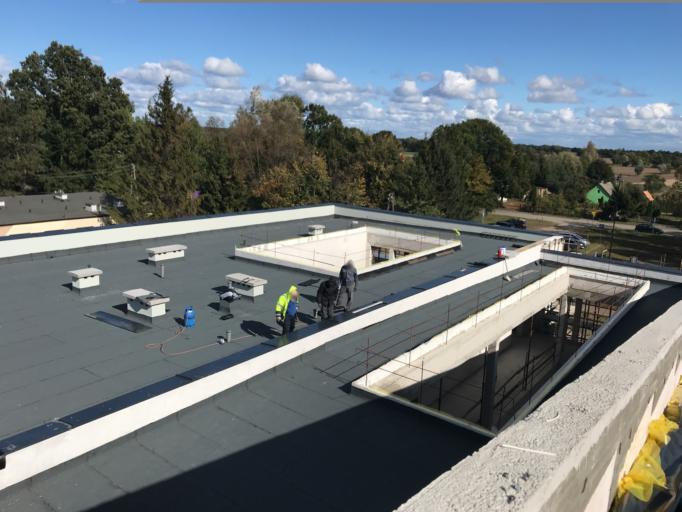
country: PL
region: Pomeranian Voivodeship
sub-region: Powiat gdanski
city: Cedry Wielkie
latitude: 54.2483
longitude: 18.8450
